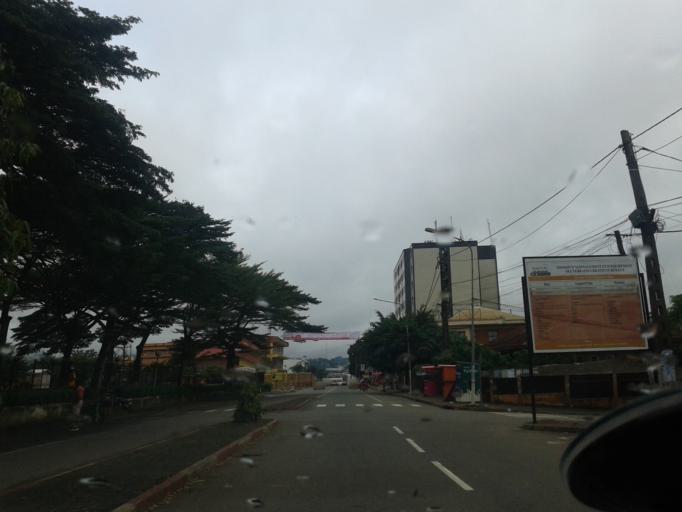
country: CM
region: Centre
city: Yaounde
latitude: 3.8753
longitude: 11.5173
